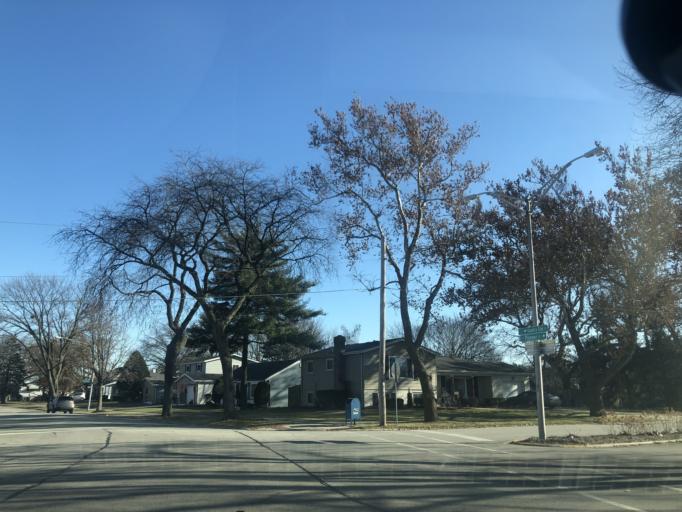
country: US
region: Illinois
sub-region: DuPage County
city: Addison
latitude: 41.9306
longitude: -88.0110
